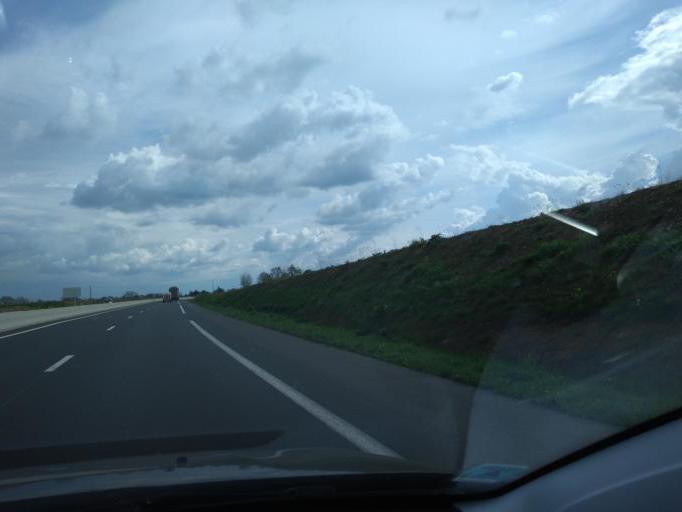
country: FR
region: Pays de la Loire
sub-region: Departement de Maine-et-Loire
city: Grez-Neuville
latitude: 47.6055
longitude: -0.7045
